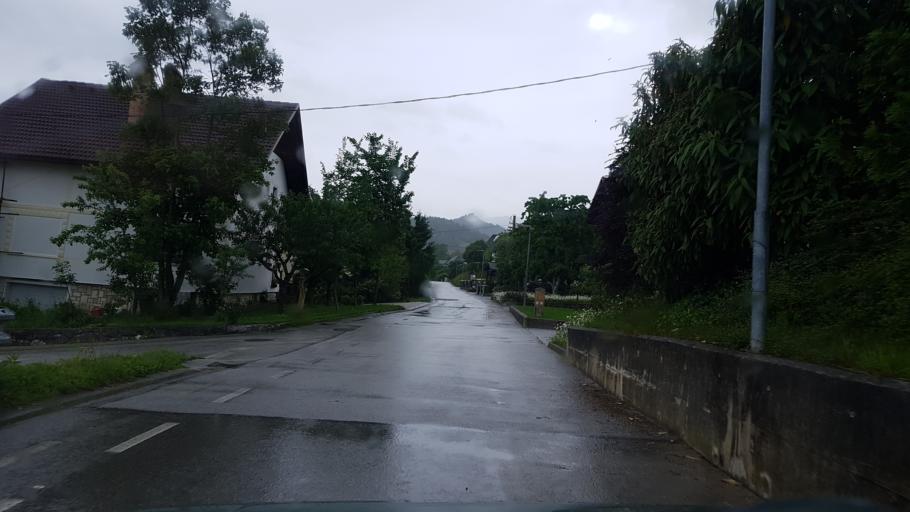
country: SI
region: Bled
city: Zasip
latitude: 46.3873
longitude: 14.0971
